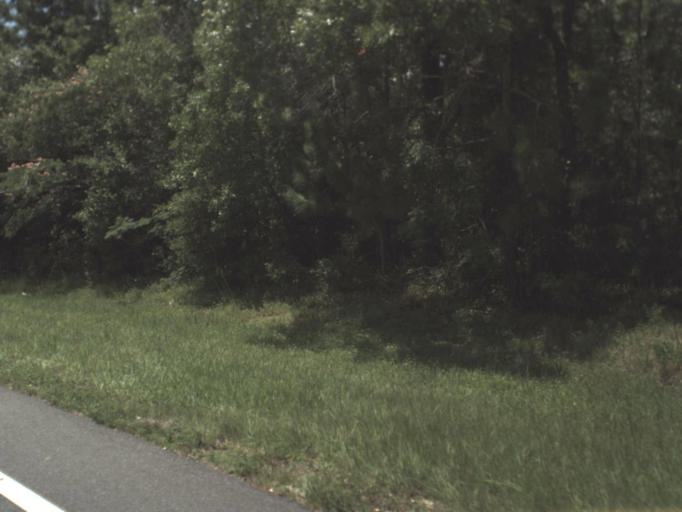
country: US
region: Florida
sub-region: Clay County
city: Keystone Heights
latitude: 29.7557
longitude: -81.9974
